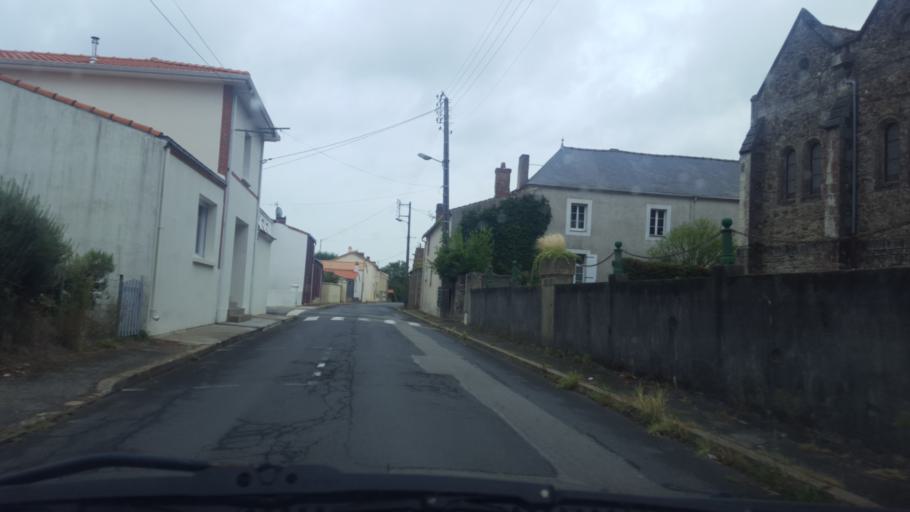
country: FR
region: Pays de la Loire
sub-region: Departement de la Loire-Atlantique
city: Saint-Lumine-de-Coutais
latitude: 47.0557
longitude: -1.7257
